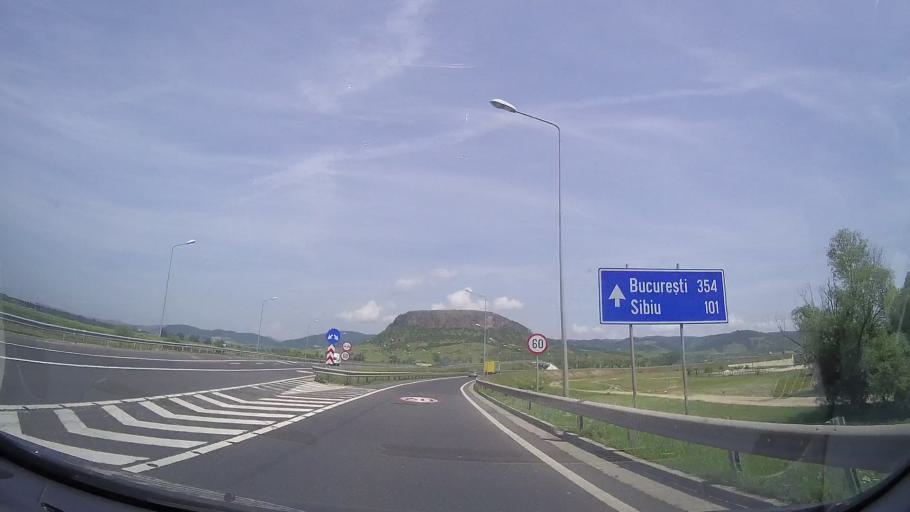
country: RO
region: Hunedoara
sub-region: Oras Simeria
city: Simeria
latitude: 45.8445
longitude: 23.0450
